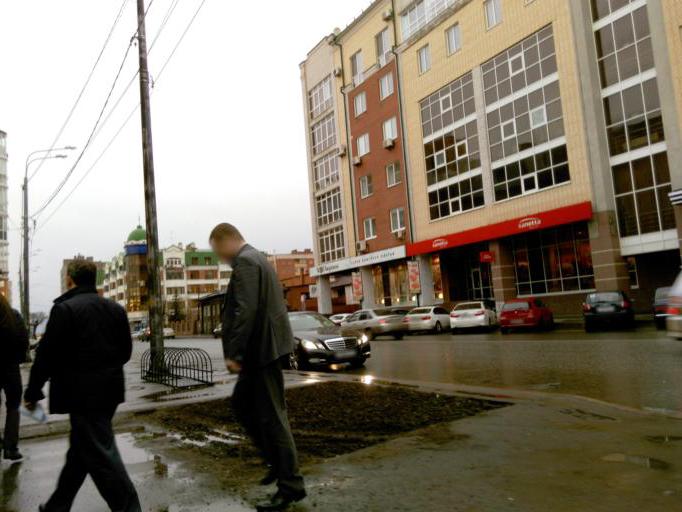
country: RU
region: Tjumen
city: Tyumen
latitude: 57.1567
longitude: 65.5444
